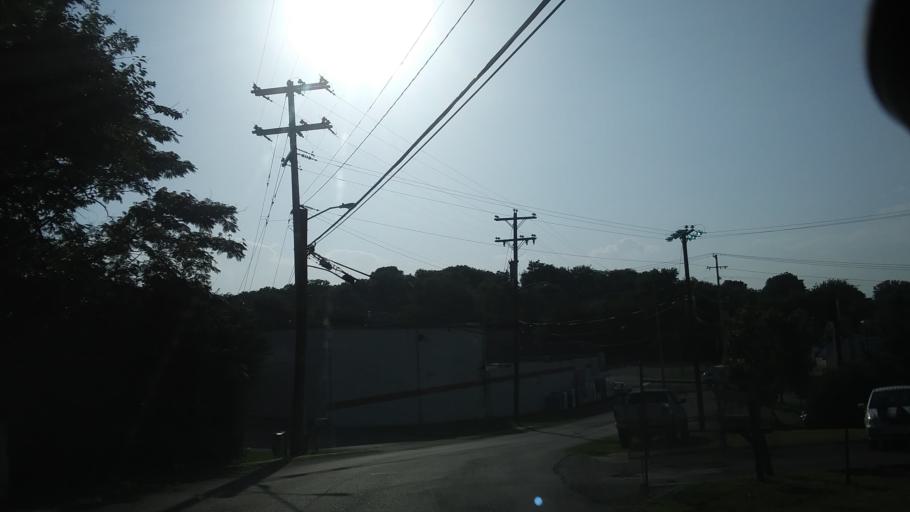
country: US
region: Tennessee
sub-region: Davidson County
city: Belle Meade
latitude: 36.1435
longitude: -86.8721
